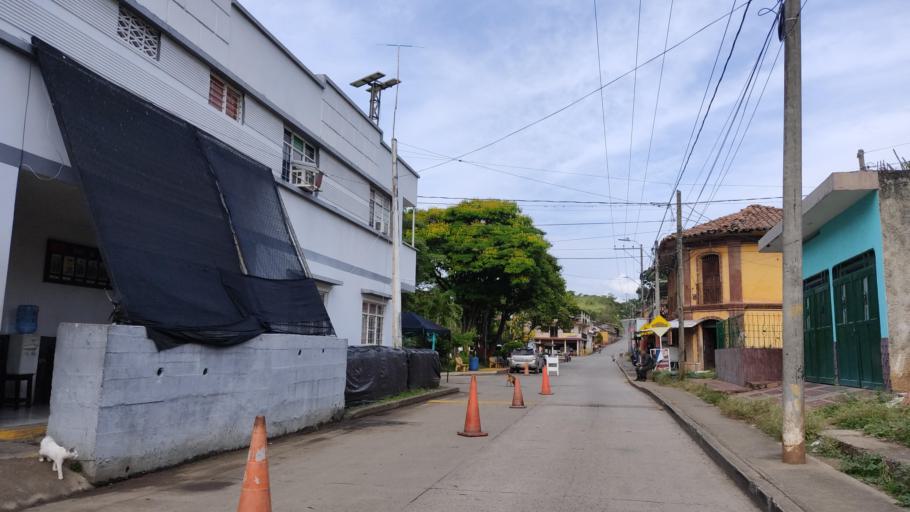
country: CO
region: Cauca
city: Buenos Aires
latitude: 3.1298
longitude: -76.5940
